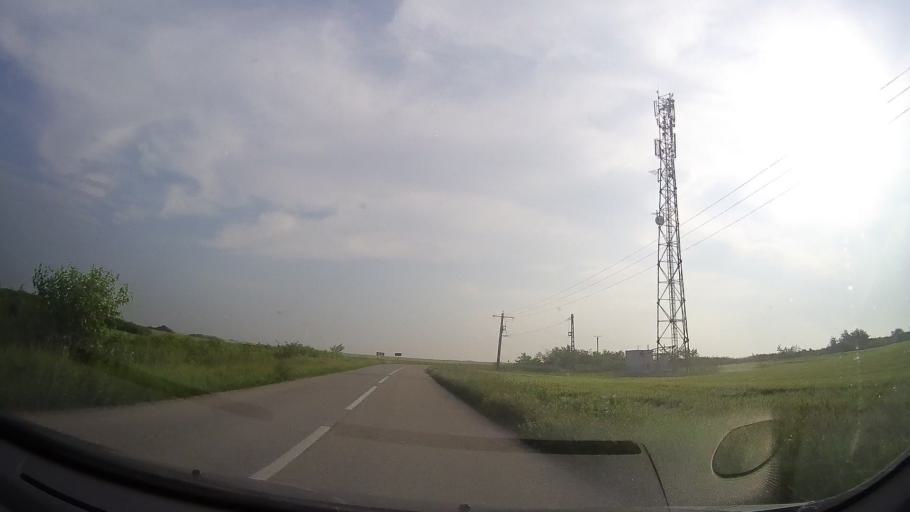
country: RO
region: Timis
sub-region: Comuna Foeni
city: Foeni
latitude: 45.5159
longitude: 20.8960
